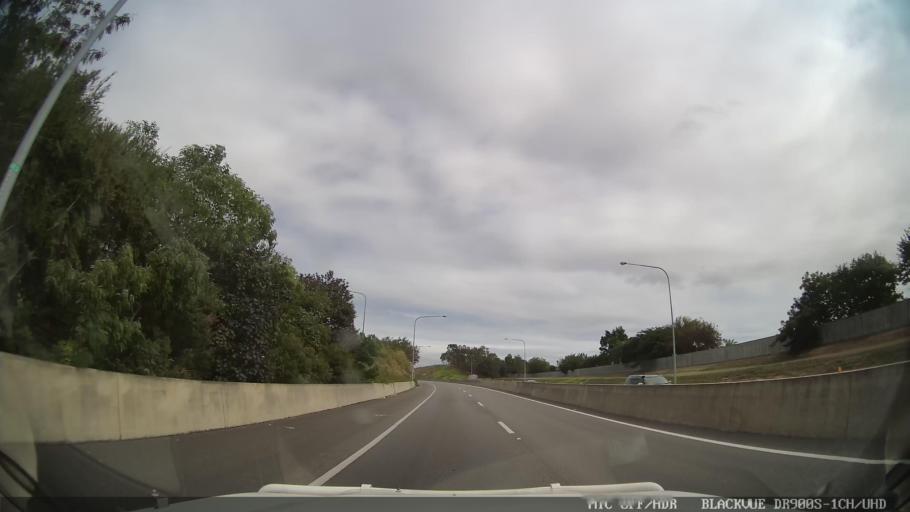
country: AU
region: Queensland
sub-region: Townsville
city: Bohle Plains
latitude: -19.3212
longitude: 146.7451
